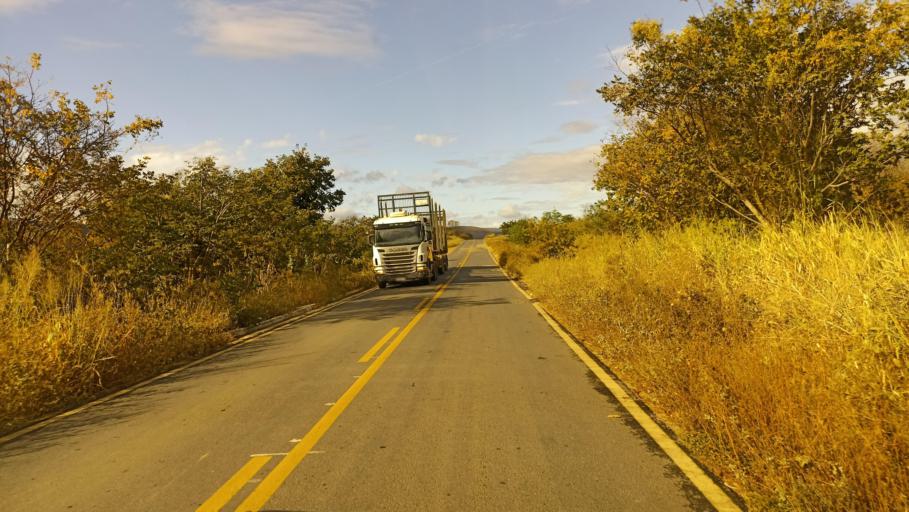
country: BR
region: Minas Gerais
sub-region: Itinga
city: Itinga
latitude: -16.5800
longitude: -41.6143
